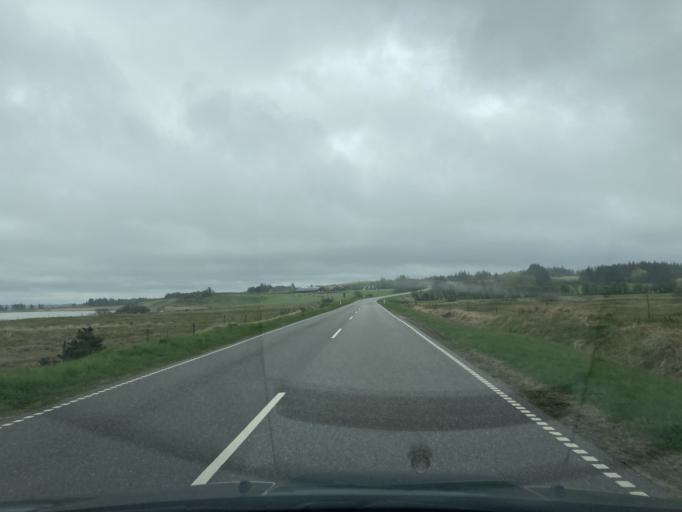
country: DK
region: North Denmark
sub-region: Thisted Kommune
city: Hurup
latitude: 56.8857
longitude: 8.3887
